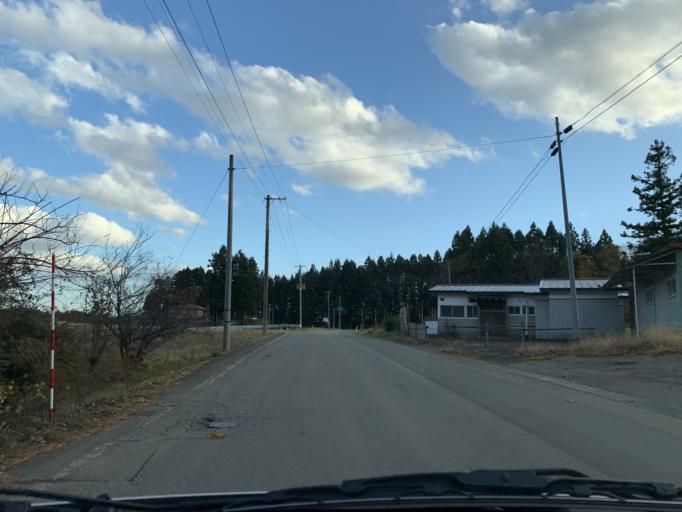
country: JP
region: Iwate
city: Mizusawa
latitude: 39.1172
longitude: 141.0373
